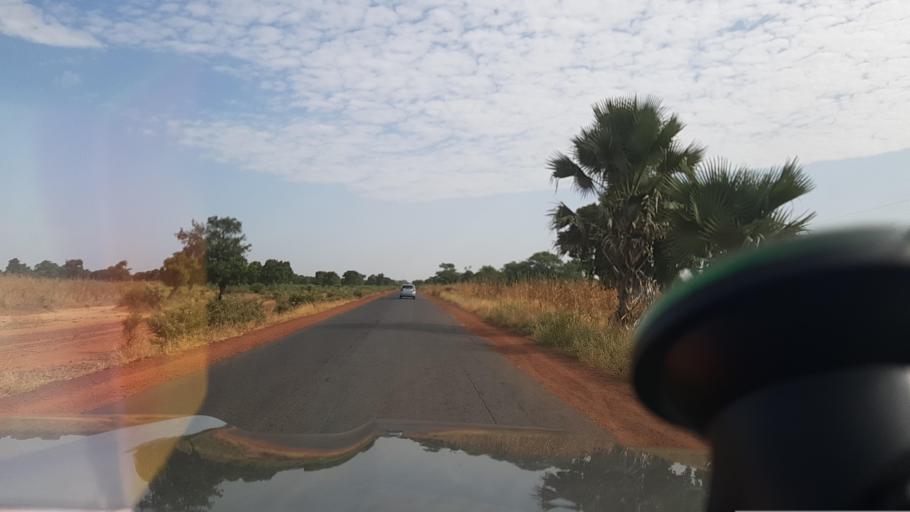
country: ML
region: Segou
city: Segou
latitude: 13.5114
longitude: -6.1423
